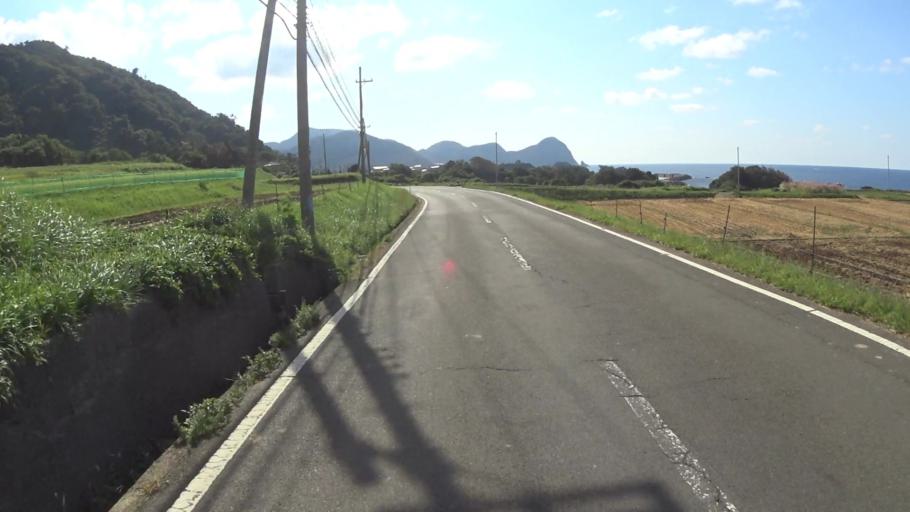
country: JP
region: Kyoto
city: Miyazu
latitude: 35.7617
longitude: 135.1882
